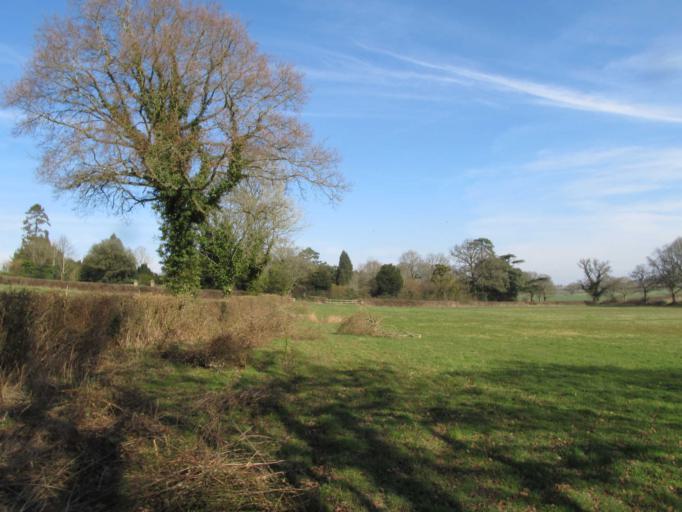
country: GB
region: England
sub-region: West Sussex
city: Petworth
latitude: 50.9908
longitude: -0.6074
